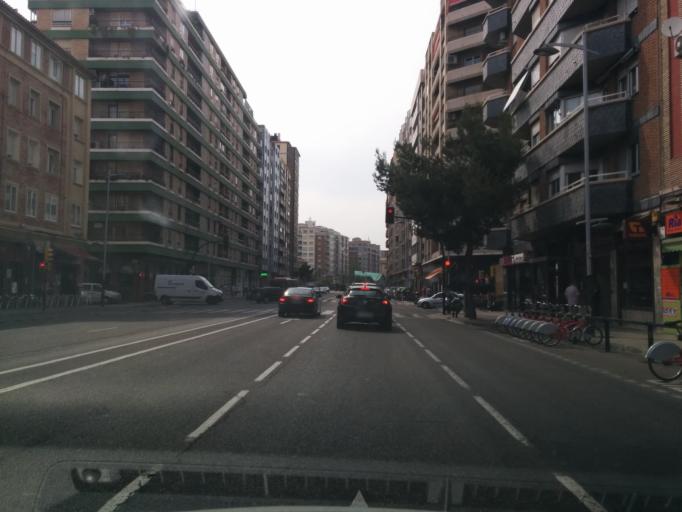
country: ES
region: Aragon
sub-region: Provincia de Zaragoza
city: Zaragoza
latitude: 41.6428
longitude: -0.8877
